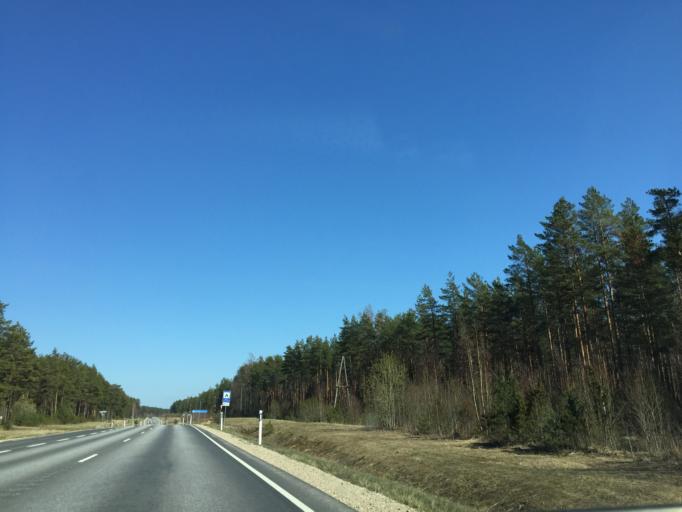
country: EE
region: Jogevamaa
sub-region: Mustvee linn
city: Mustvee
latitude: 58.9702
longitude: 27.1181
